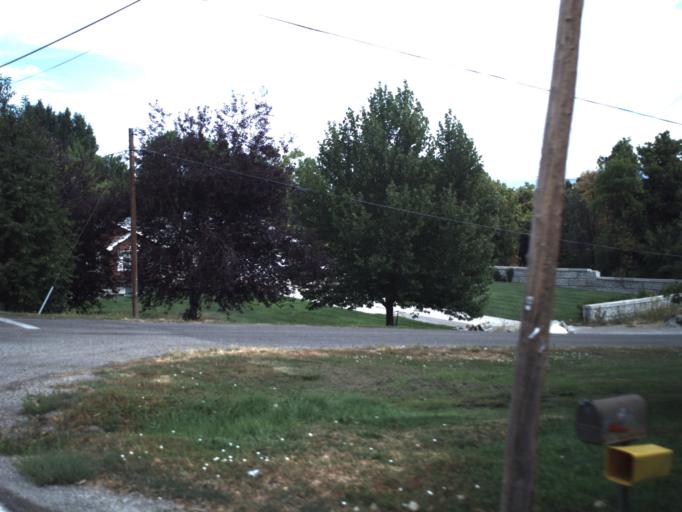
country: US
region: Utah
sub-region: Cache County
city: Mendon
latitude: 41.7140
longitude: -111.9790
